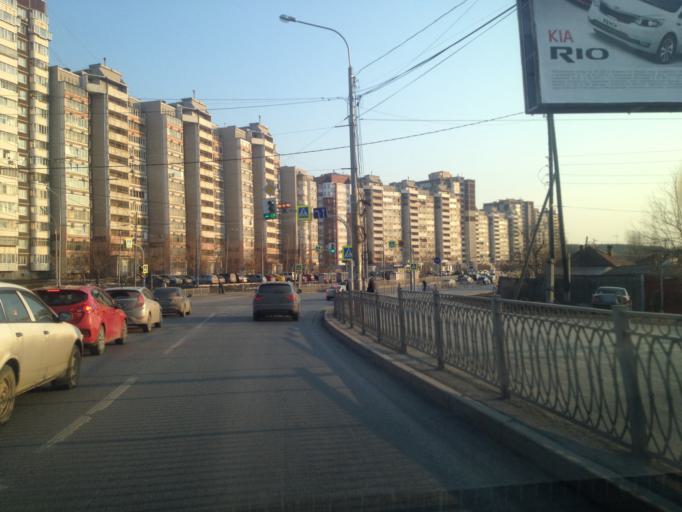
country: RU
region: Sverdlovsk
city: Sovkhoznyy
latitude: 56.8250
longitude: 60.5434
